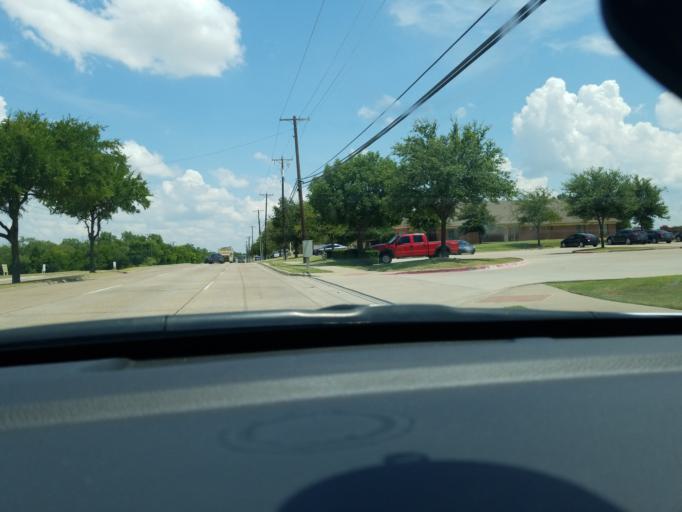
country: US
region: Texas
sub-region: Dallas County
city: Sunnyvale
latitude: 32.8037
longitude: -96.5957
